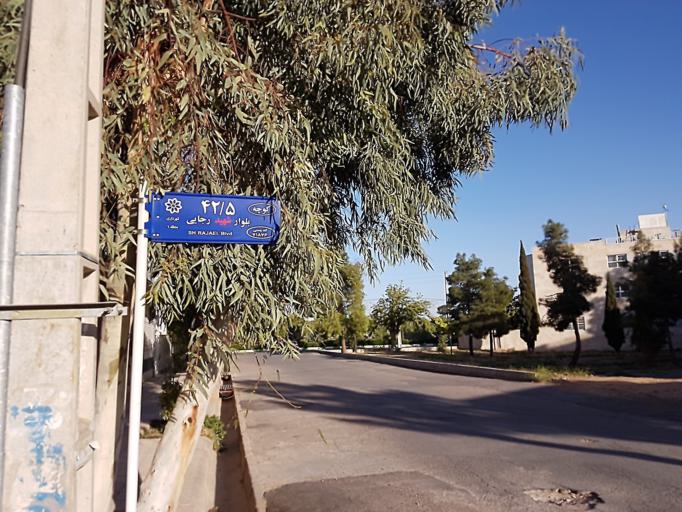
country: IR
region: Fars
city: Shiraz
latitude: 29.6657
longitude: 52.4575
